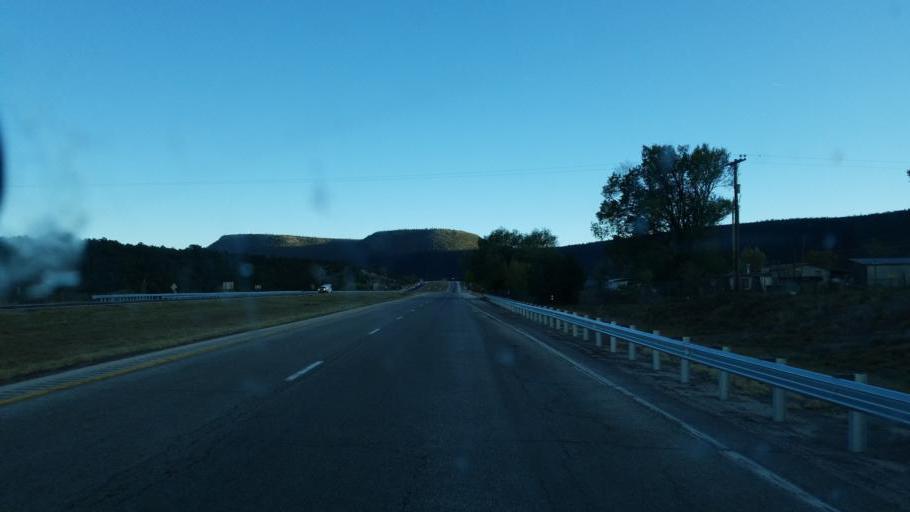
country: US
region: New Mexico
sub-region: San Miguel County
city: Pecos
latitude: 35.4922
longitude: -105.6726
